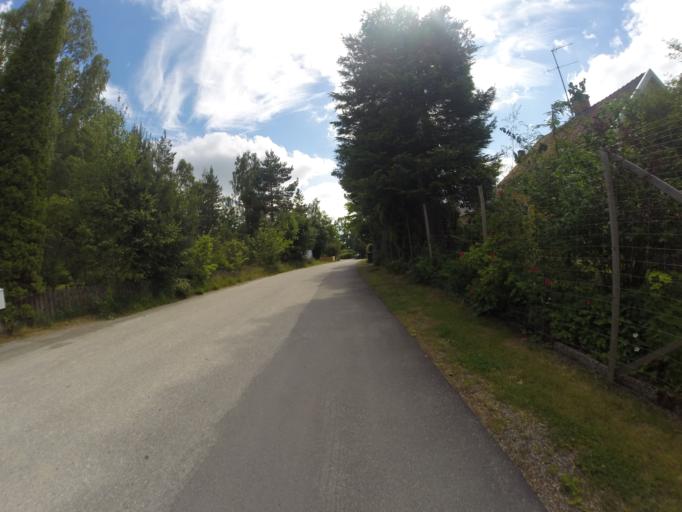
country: SE
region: Soedermanland
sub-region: Eskilstuna Kommun
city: Skogstorp
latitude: 59.3308
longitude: 16.4848
